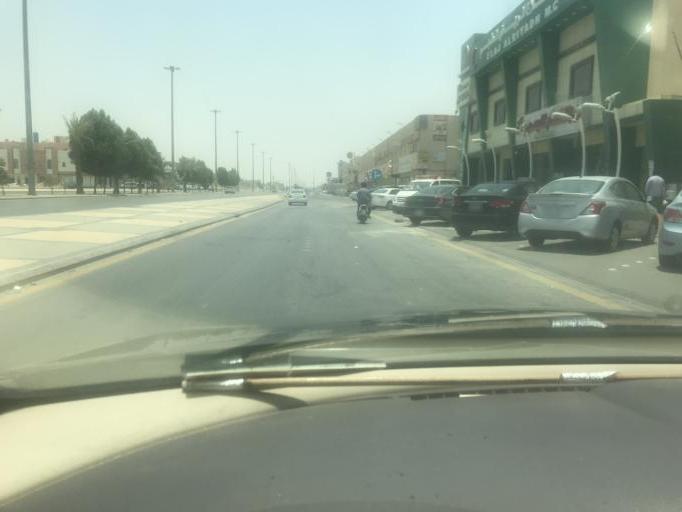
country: SA
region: Ar Riyad
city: Riyadh
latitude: 24.8180
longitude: 46.7525
